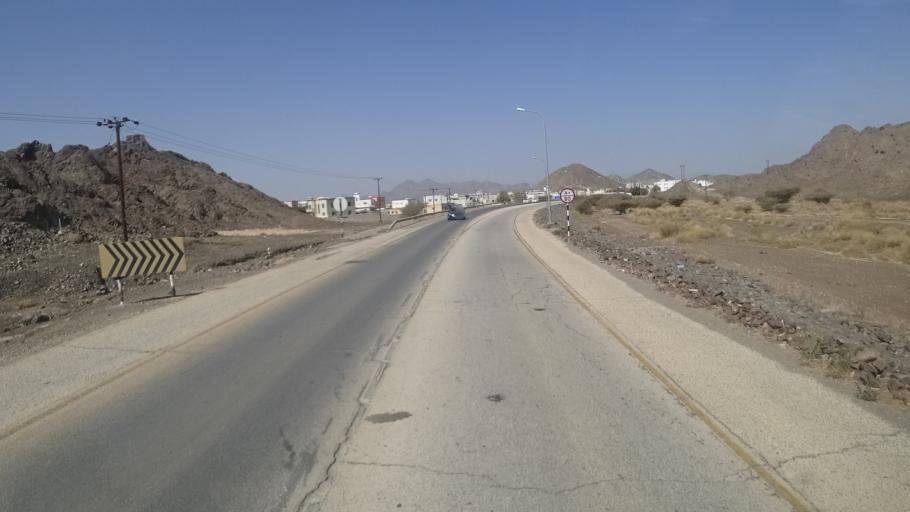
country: OM
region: Ash Sharqiyah
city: Ibra'
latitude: 22.6834
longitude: 58.5582
